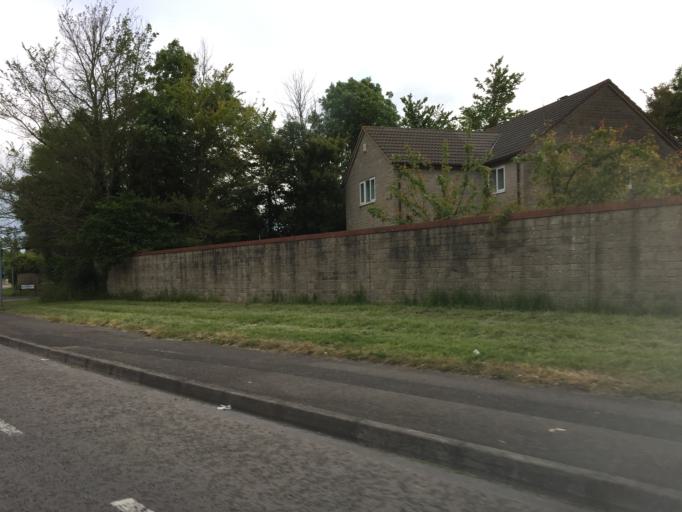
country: GB
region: England
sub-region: South Gloucestershire
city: Almondsbury
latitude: 51.5388
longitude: -2.5598
